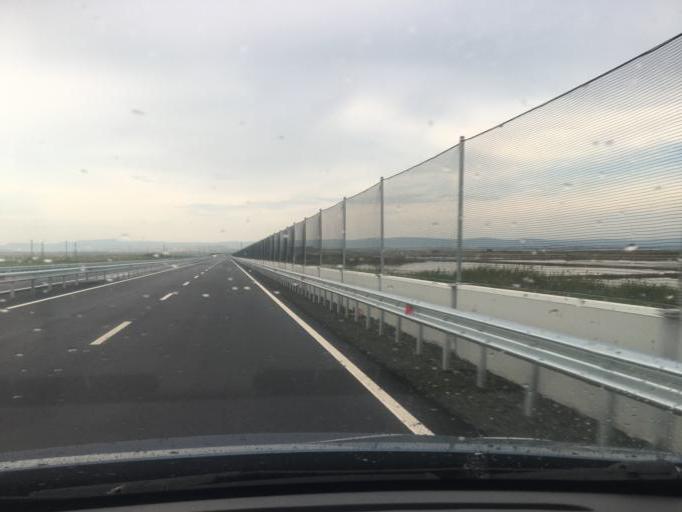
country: BG
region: Burgas
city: Aheloy
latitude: 42.6088
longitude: 27.6215
